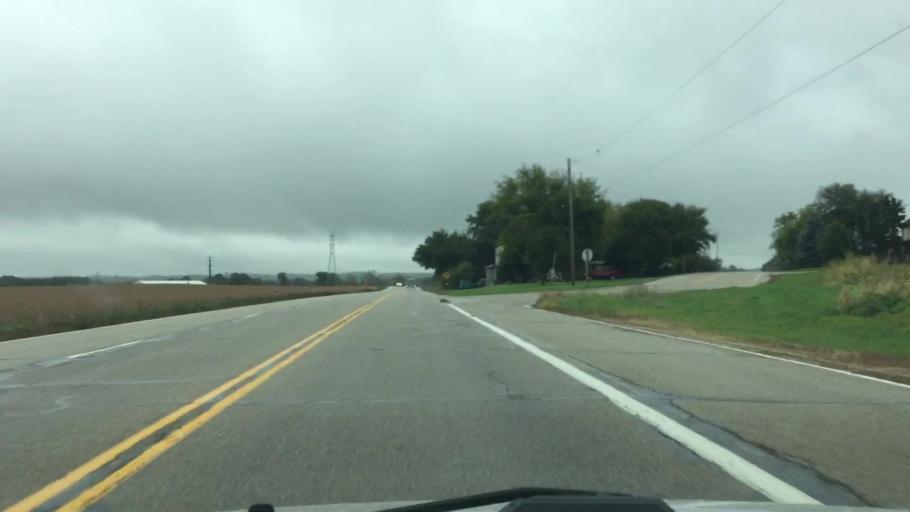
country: US
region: Wisconsin
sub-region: Walworth County
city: Whitewater
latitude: 42.8252
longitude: -88.7041
